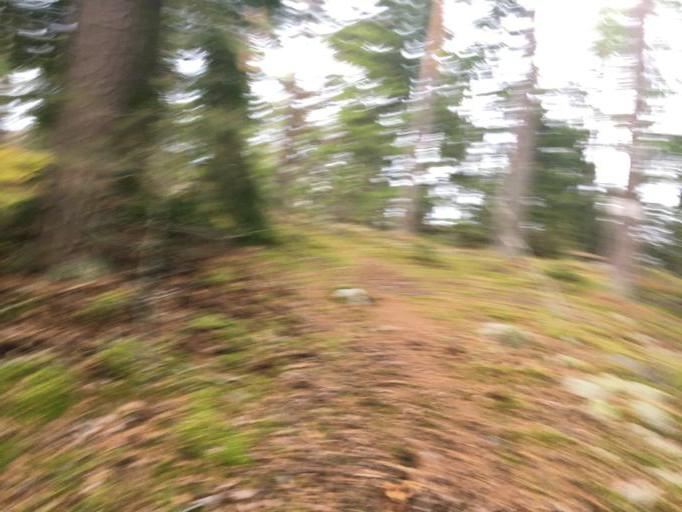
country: SE
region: Soedermanland
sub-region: Eskilstuna Kommun
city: Eskilstuna
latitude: 59.4569
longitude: 16.6610
